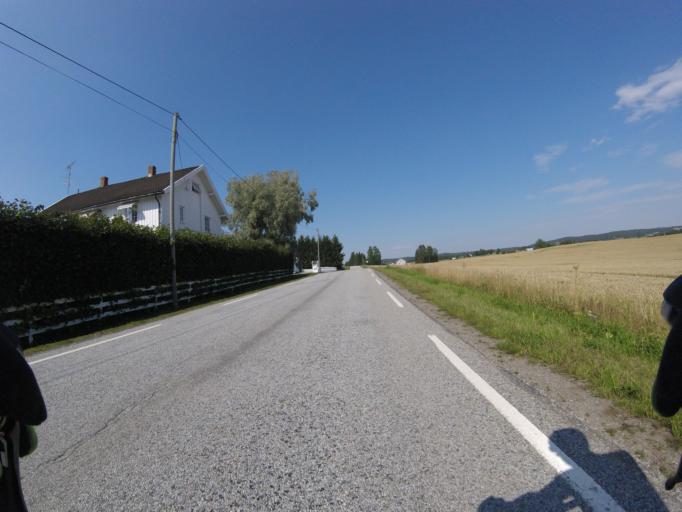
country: NO
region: Akershus
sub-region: Ullensaker
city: Klofta
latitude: 60.0871
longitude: 11.1621
